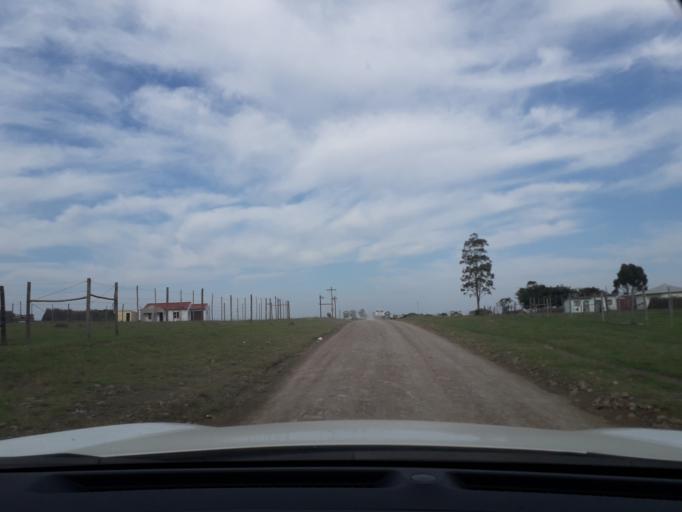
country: ZA
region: Eastern Cape
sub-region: Buffalo City Metropolitan Municipality
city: Bhisho
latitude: -32.9821
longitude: 27.3623
